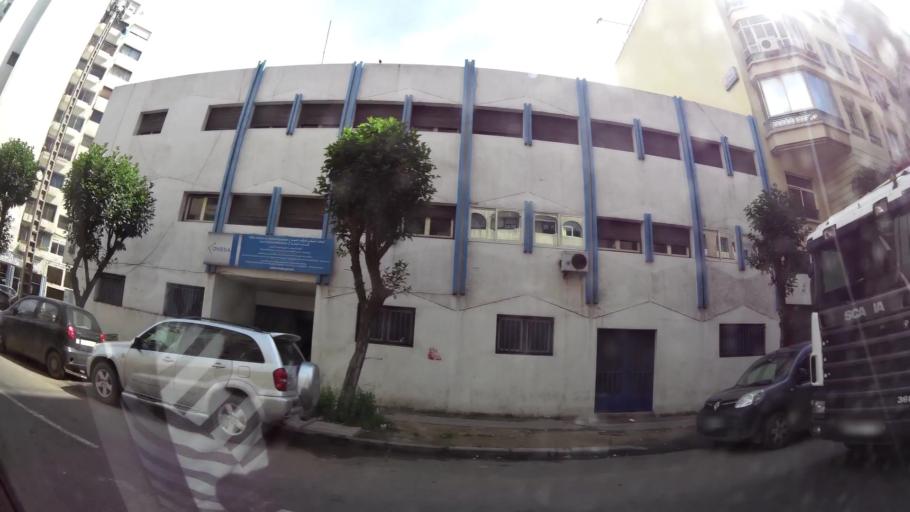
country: MA
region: Grand Casablanca
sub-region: Casablanca
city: Casablanca
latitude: 33.5880
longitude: -7.6013
